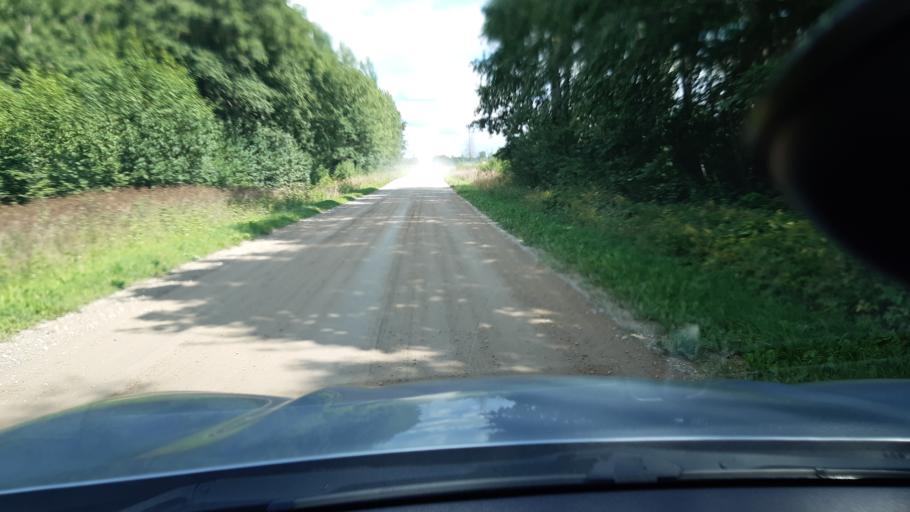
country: EE
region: Raplamaa
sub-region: Kehtna vald
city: Kehtna
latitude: 58.9112
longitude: 25.1515
